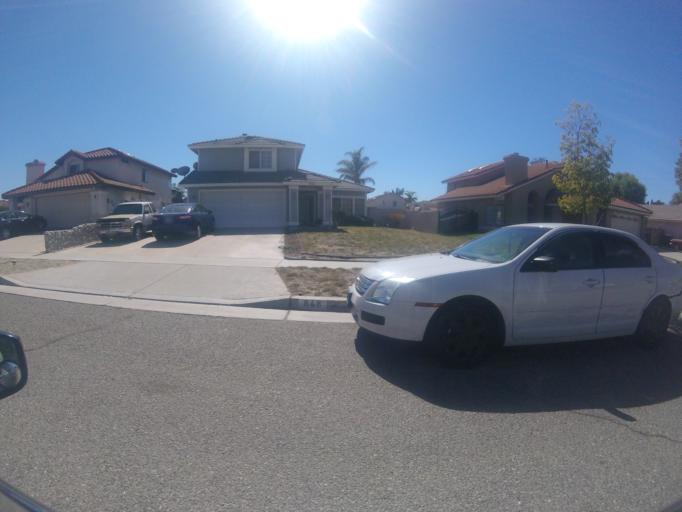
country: US
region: California
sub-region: San Bernardino County
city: Redlands
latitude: 34.0834
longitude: -117.1722
